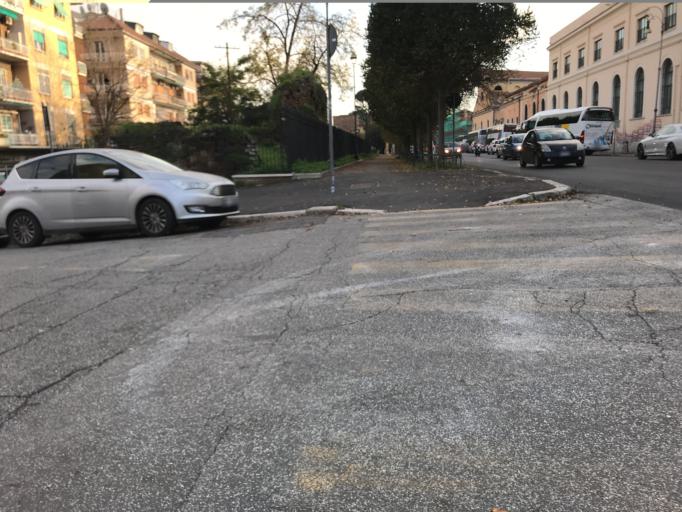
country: IT
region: Latium
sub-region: Citta metropolitana di Roma Capitale
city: Rome
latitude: 41.9006
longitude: 12.5084
